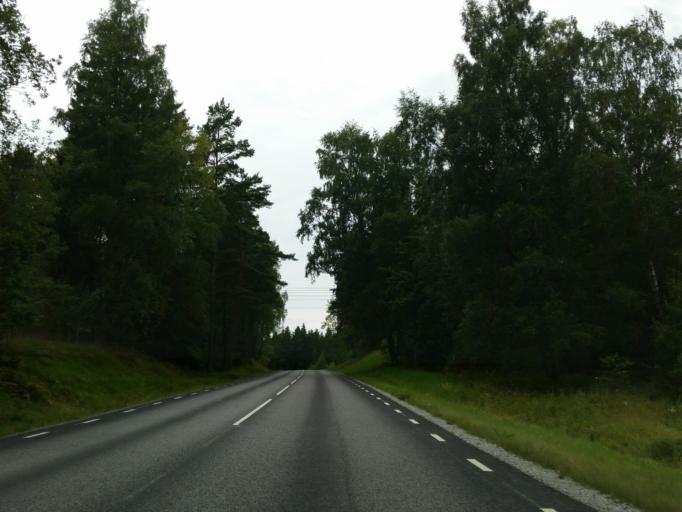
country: SE
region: Stockholm
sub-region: Salems Kommun
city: Ronninge
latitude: 59.2310
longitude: 17.6963
